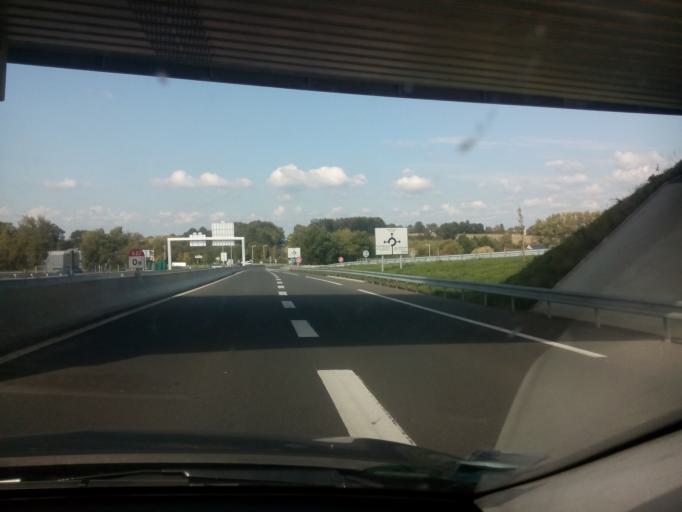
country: FR
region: Pays de la Loire
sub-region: Departement de Maine-et-Loire
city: Ecouflant
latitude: 47.5036
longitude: -0.5030
